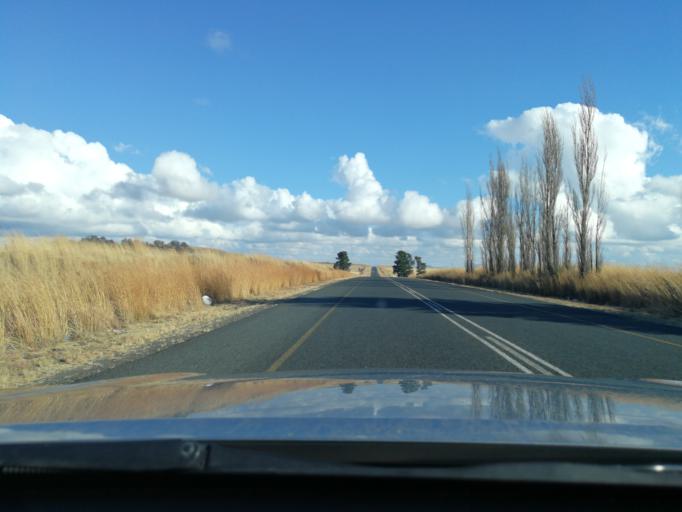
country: ZA
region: Orange Free State
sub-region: Thabo Mofutsanyana District Municipality
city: Bethlehem
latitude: -28.0716
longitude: 28.3600
